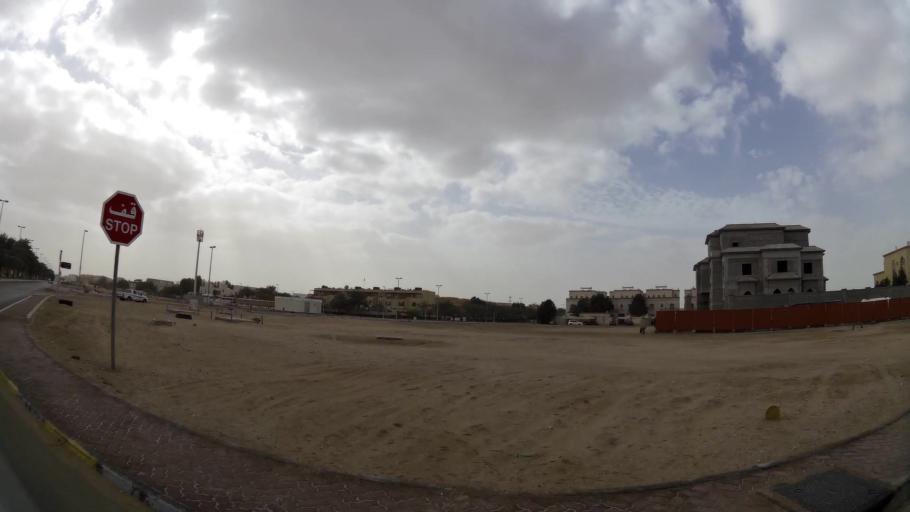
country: AE
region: Abu Dhabi
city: Abu Dhabi
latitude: 24.4149
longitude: 54.4974
